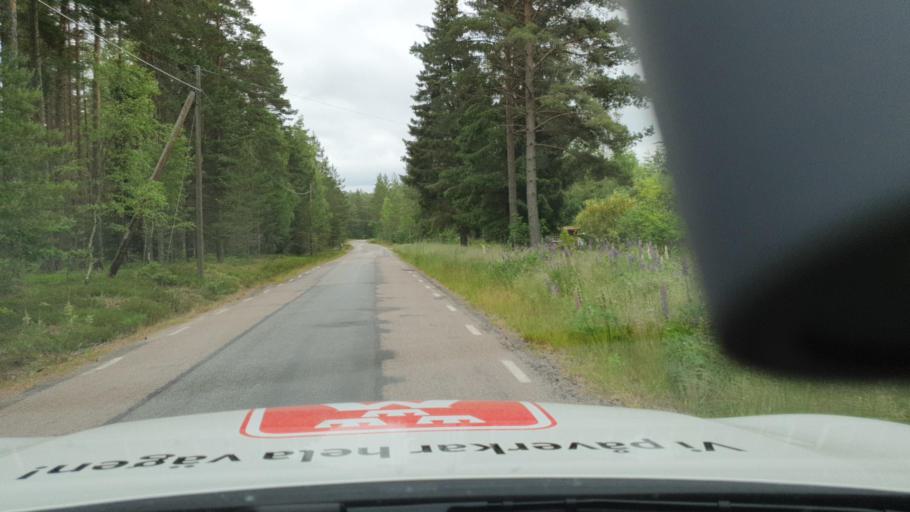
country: SE
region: Vaestra Goetaland
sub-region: Karlsborgs Kommun
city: Molltorp
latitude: 58.4271
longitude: 14.3744
